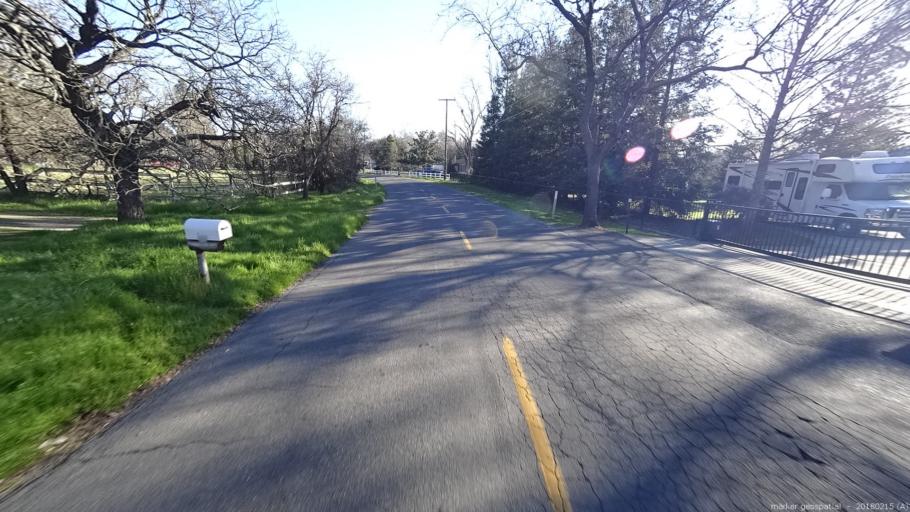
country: US
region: California
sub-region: Sacramento County
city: Foothill Farms
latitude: 38.6765
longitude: -121.3334
